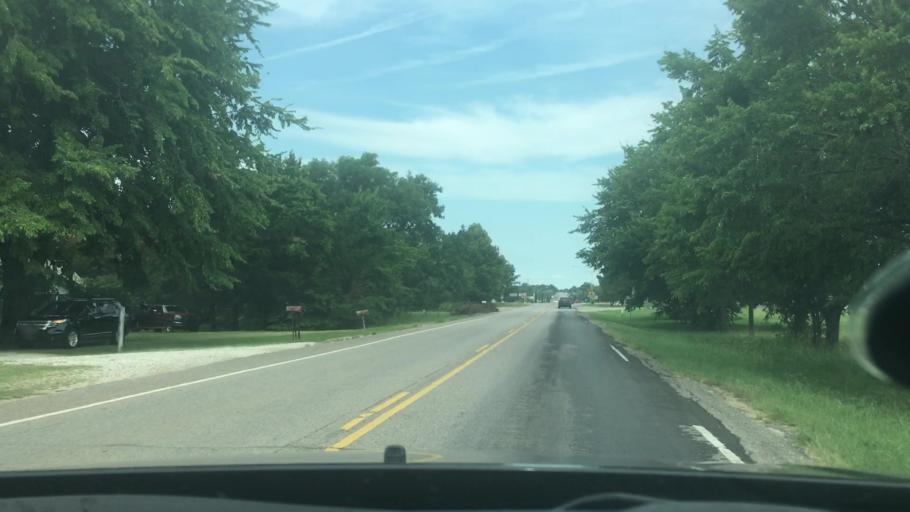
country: US
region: Oklahoma
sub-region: Seminole County
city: Seminole
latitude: 35.2436
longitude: -96.6985
